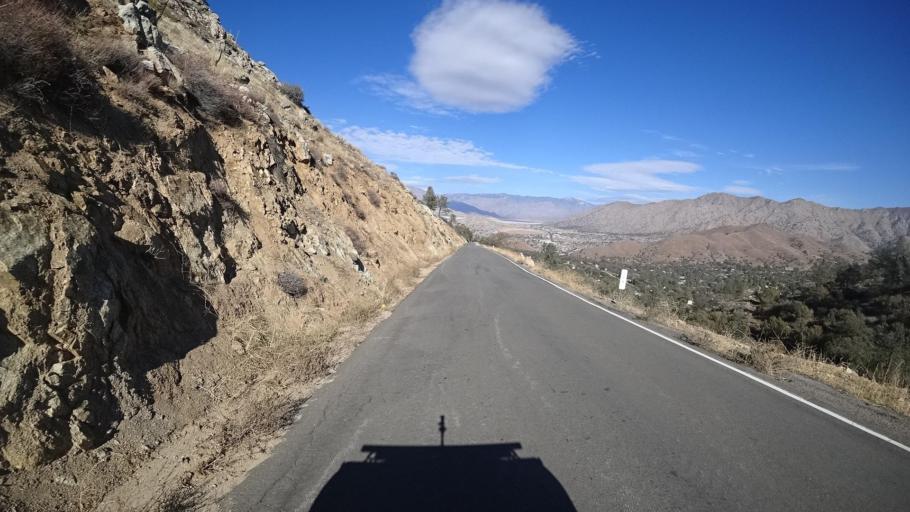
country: US
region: California
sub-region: Kern County
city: Bodfish
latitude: 35.5822
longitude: -118.5024
